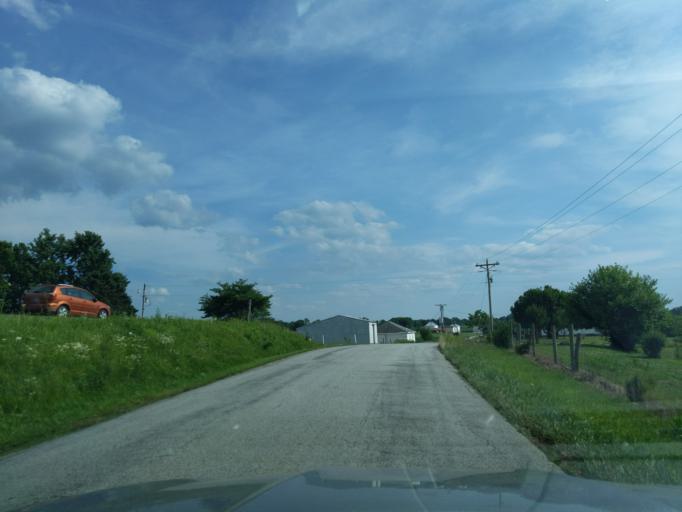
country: US
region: Indiana
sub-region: Decatur County
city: Greensburg
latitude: 39.2640
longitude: -85.4651
